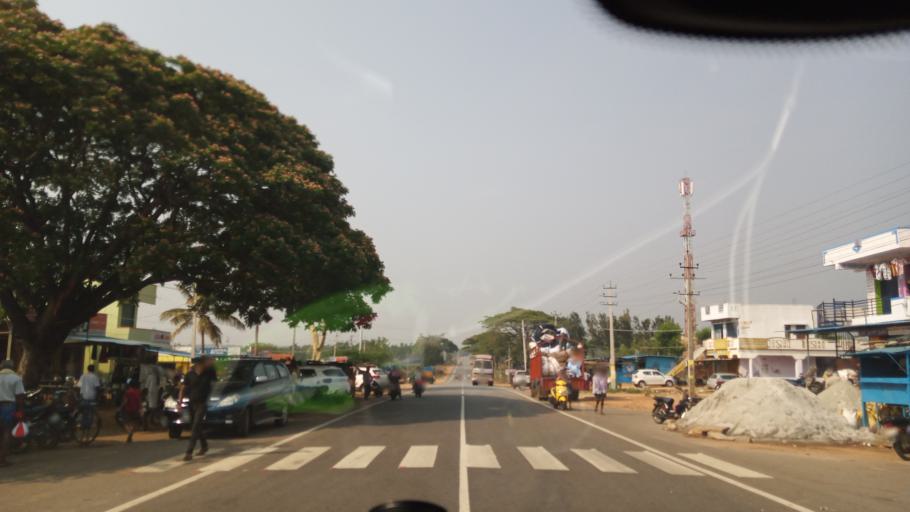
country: IN
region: Karnataka
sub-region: Mandya
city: Melukote
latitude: 12.7033
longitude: 76.7003
